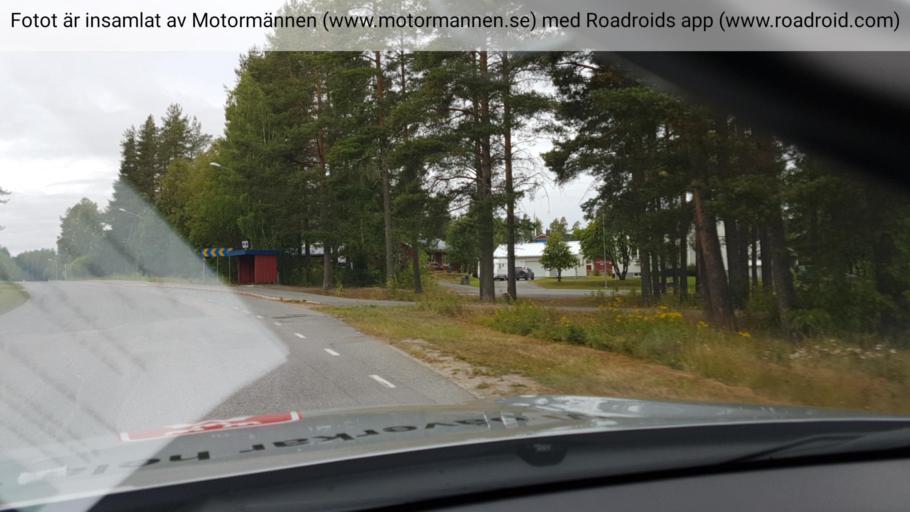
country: SE
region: Norrbotten
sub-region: Bodens Kommun
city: Boden
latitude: 65.8152
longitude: 21.6145
